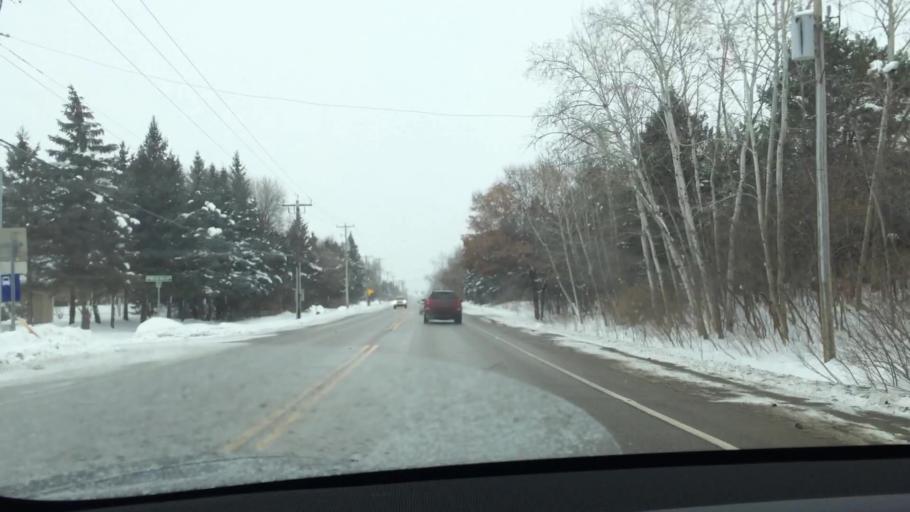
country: US
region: Minnesota
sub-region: Ramsey County
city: Shoreview
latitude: 45.1036
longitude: -93.1273
